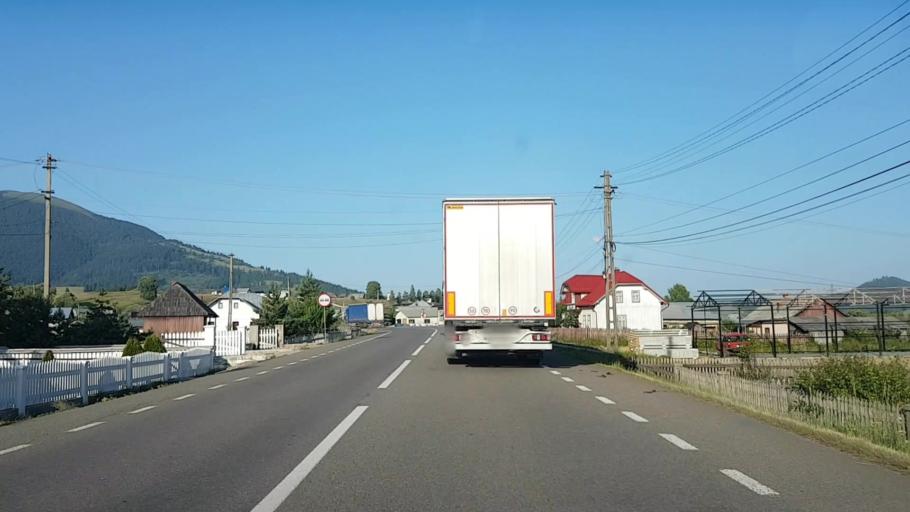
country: RO
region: Suceava
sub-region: Comuna Cosna
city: Cosna
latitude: 47.3608
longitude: 25.2002
